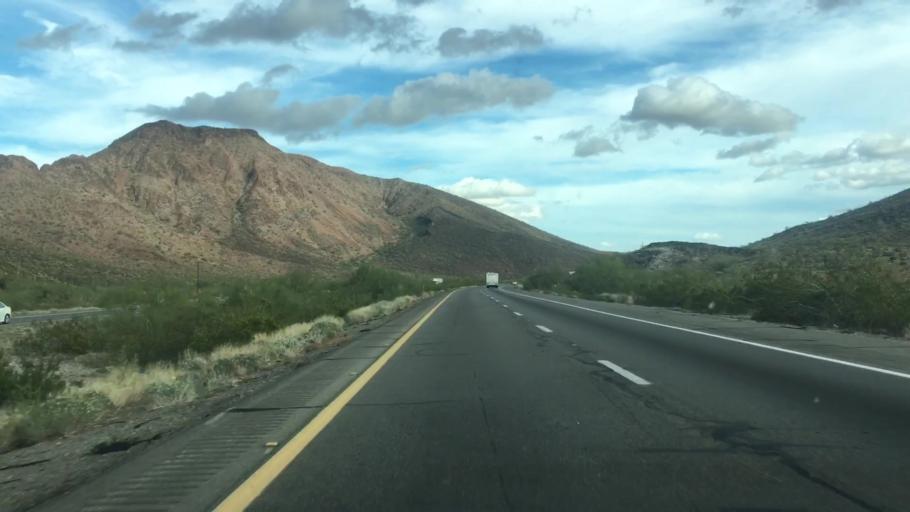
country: US
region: Arizona
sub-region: La Paz County
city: Quartzsite
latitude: 33.6770
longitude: -114.0620
